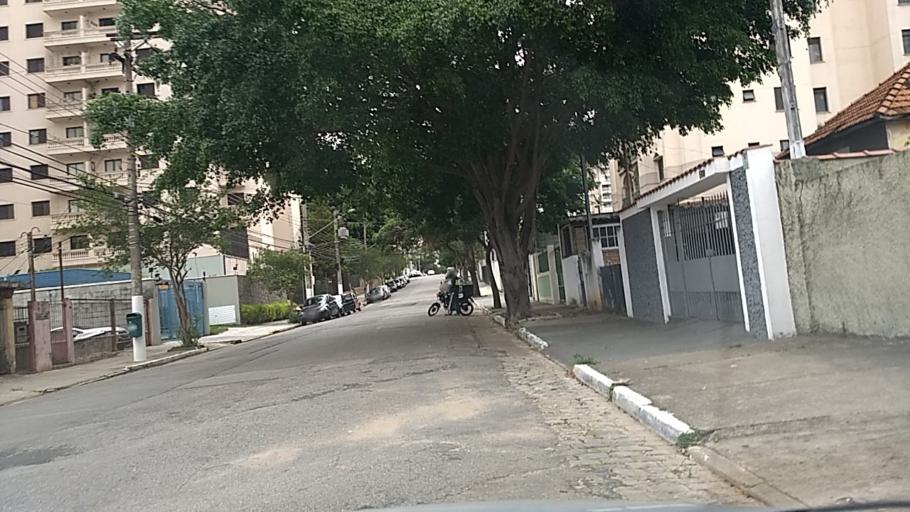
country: BR
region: Sao Paulo
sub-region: Sao Paulo
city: Sao Paulo
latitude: -23.6160
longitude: -46.6303
